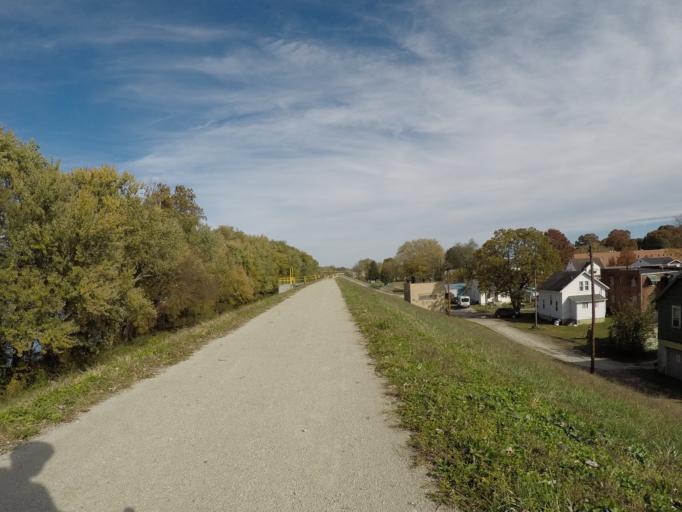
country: US
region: Ohio
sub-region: Lawrence County
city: Burlington
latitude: 38.4111
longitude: -82.4931
